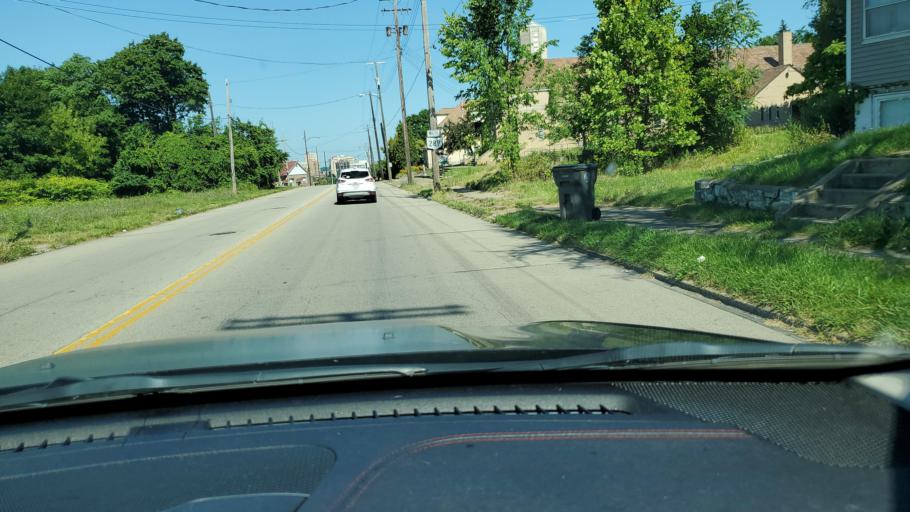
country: US
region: Ohio
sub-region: Mahoning County
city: Youngstown
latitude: 41.0916
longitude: -80.6322
